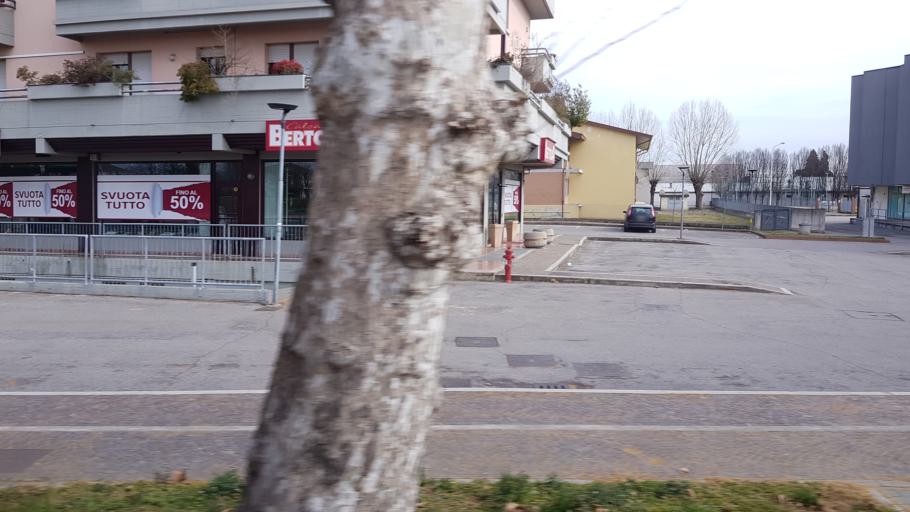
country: IT
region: Veneto
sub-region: Provincia di Padova
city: Campodarsego
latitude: 45.5005
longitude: 11.9067
